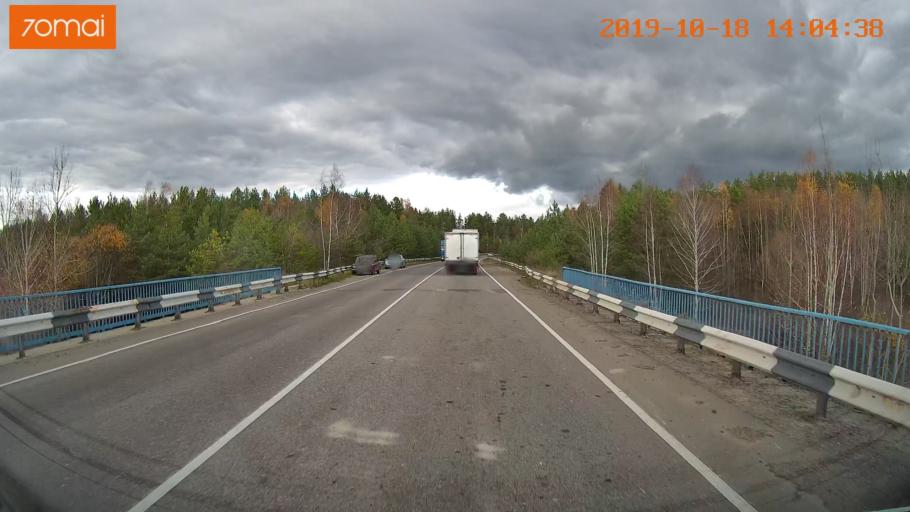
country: RU
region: Rjazan
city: Spas-Klepiki
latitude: 55.1279
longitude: 40.1335
